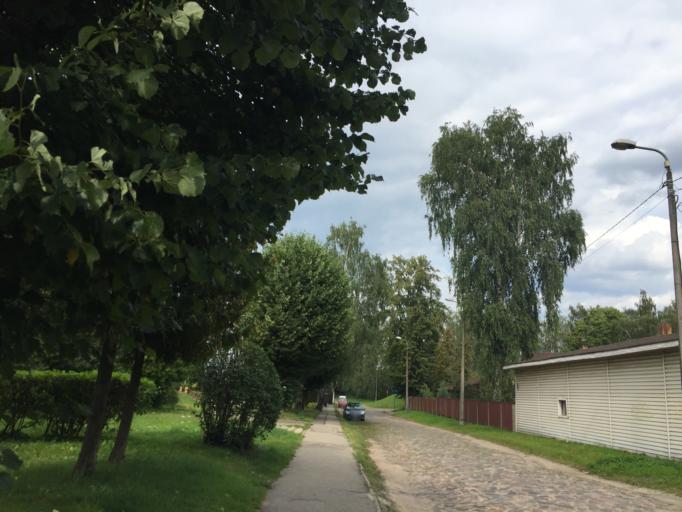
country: LV
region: Riga
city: Riga
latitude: 56.9313
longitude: 24.0884
